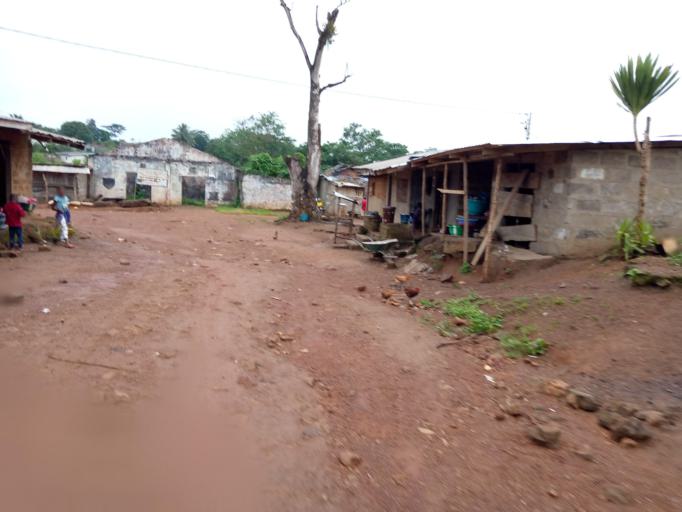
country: SL
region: Eastern Province
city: Buedu
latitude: 8.4634
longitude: -10.3386
